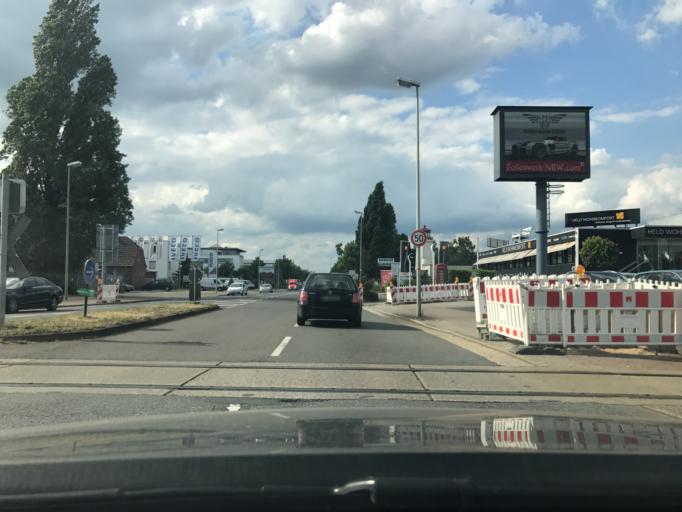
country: DE
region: North Rhine-Westphalia
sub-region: Regierungsbezirk Dusseldorf
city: Krefeld
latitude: 51.3231
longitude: 6.5938
